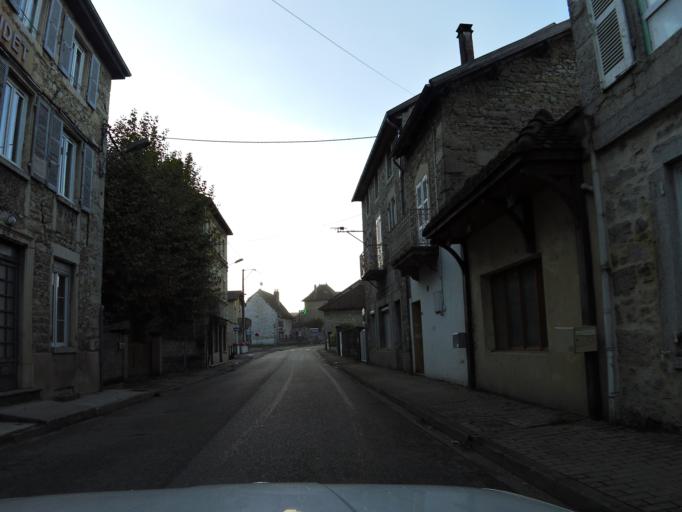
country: FR
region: Rhone-Alpes
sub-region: Departement de l'Isere
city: Bouvesse-Quirieu
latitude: 45.8066
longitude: 5.4537
